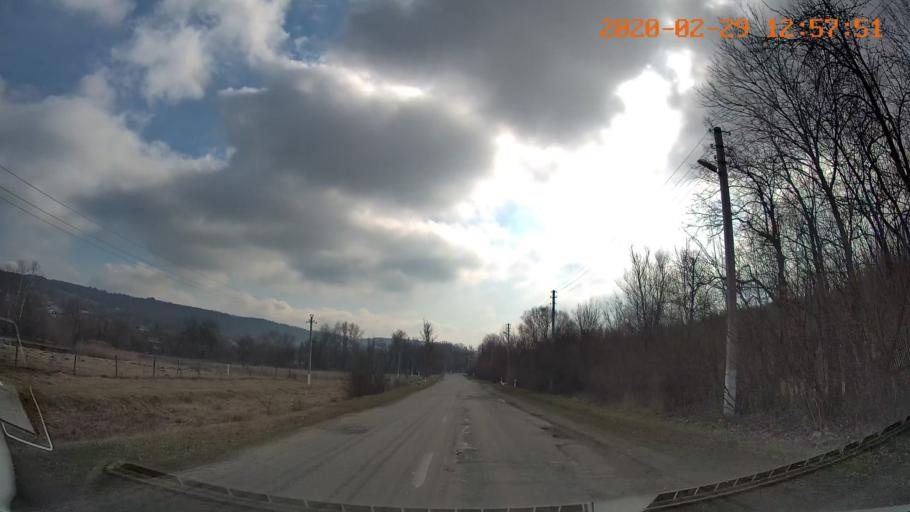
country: MD
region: Telenesti
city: Camenca
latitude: 48.0740
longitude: 28.7170
